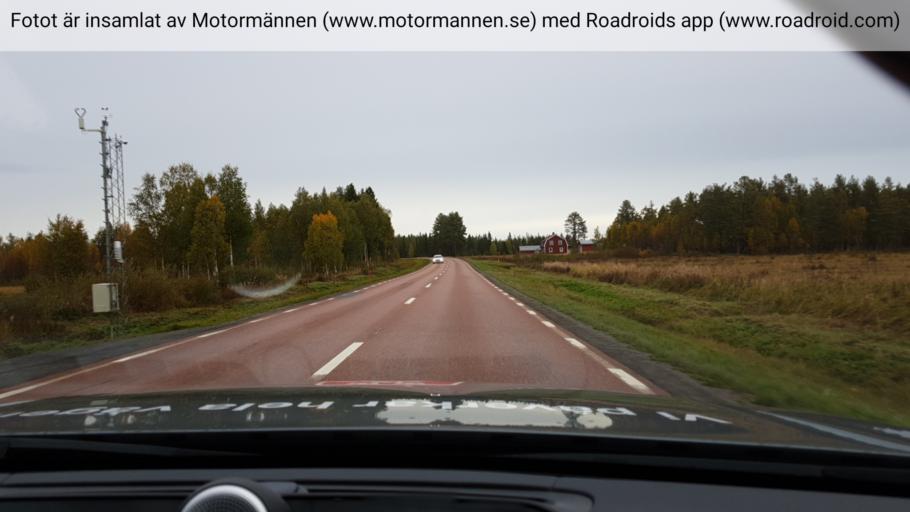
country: SE
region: Jaemtland
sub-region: Stroemsunds Kommun
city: Stroemsund
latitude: 63.7449
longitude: 15.4917
